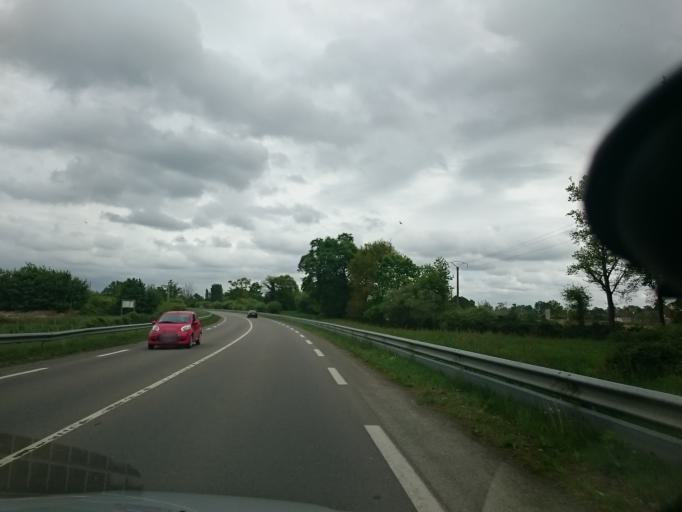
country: FR
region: Brittany
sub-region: Departement d'Ille-et-Vilaine
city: Saint-Brice-en-Cogles
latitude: 48.3969
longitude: -1.3696
